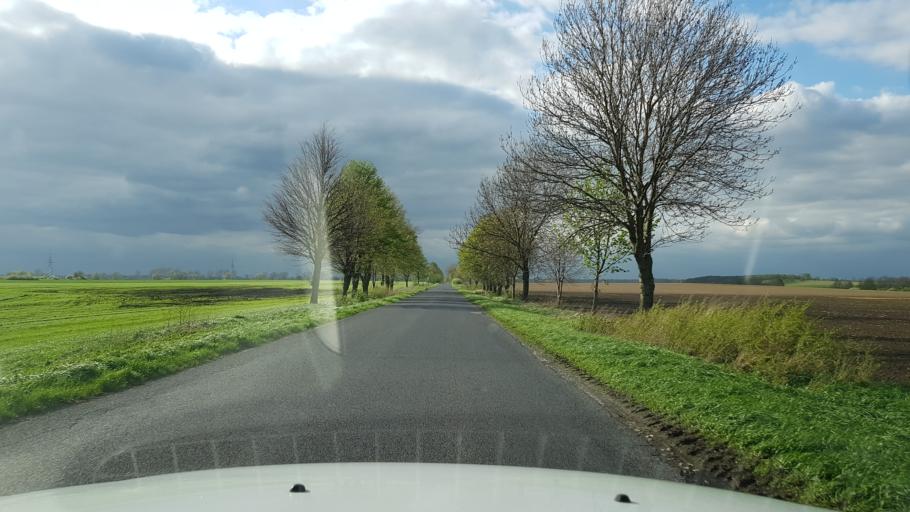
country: PL
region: West Pomeranian Voivodeship
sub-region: Powiat pyrzycki
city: Przelewice
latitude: 53.1287
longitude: 15.0495
